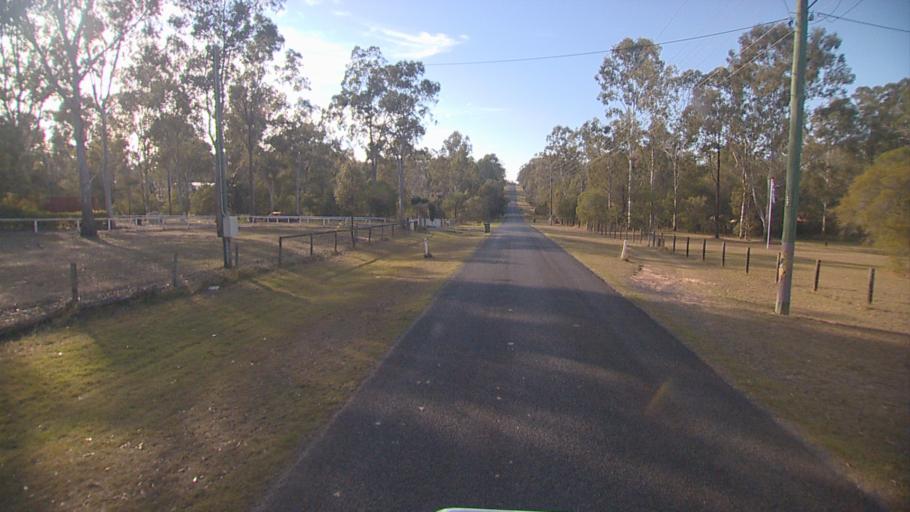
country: AU
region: Queensland
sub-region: Logan
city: North Maclean
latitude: -27.7558
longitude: 152.9975
